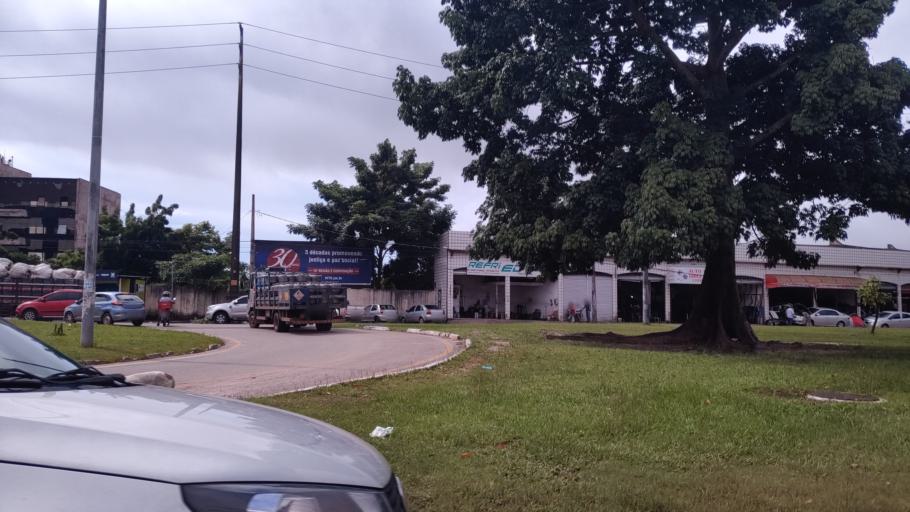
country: BR
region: Maranhao
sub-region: Sao Luis
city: Sao Luis
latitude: -2.5411
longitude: -44.2884
